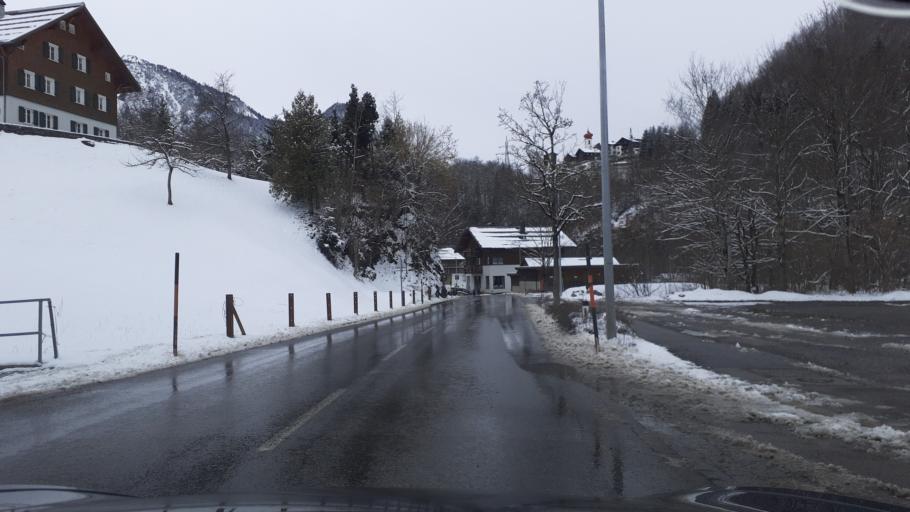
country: AT
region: Vorarlberg
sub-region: Politischer Bezirk Bludenz
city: Dalaas
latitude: 47.1228
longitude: 10.0012
